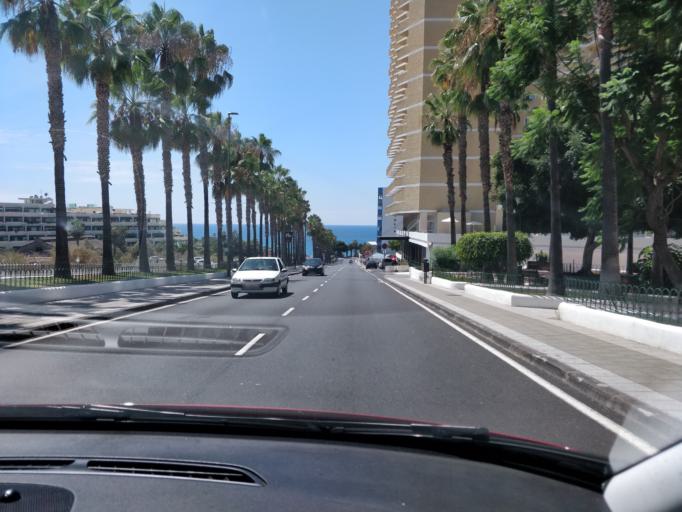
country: ES
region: Canary Islands
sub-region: Provincia de Santa Cruz de Tenerife
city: Puerto de la Cruz
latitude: 28.4110
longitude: -16.5556
